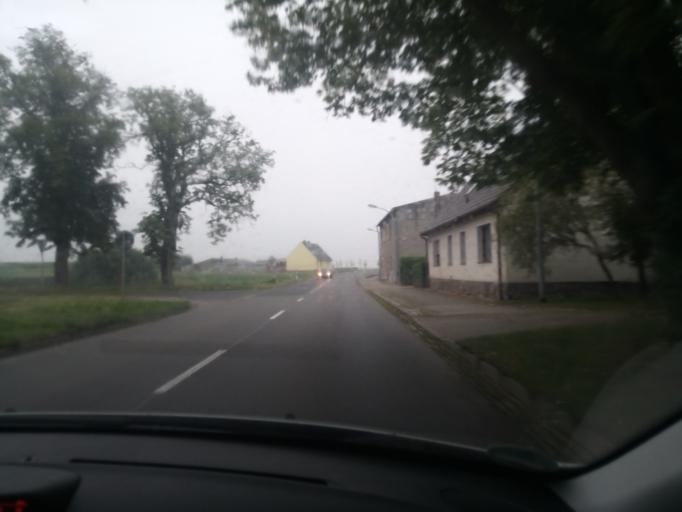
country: DE
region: Mecklenburg-Vorpommern
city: Woldegk
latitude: 53.4724
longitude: 13.6388
